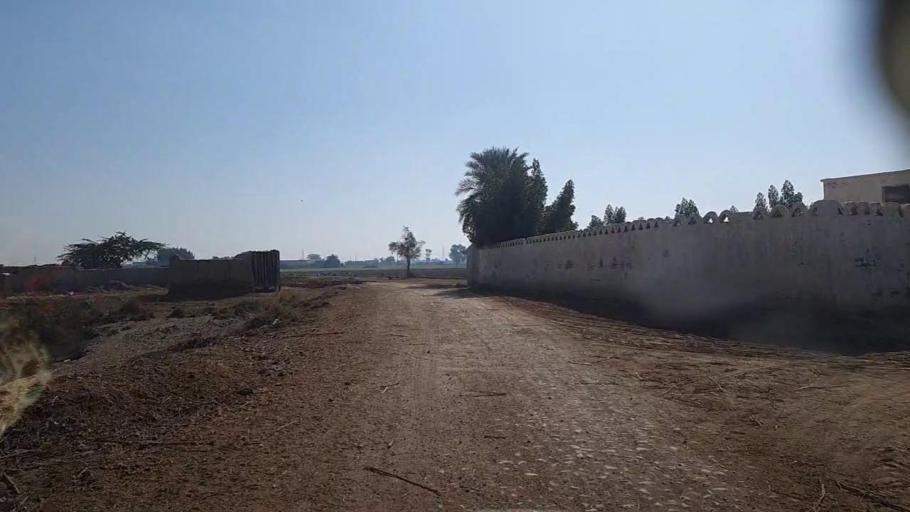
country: PK
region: Sindh
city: Khairpur
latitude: 28.0485
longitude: 69.7787
